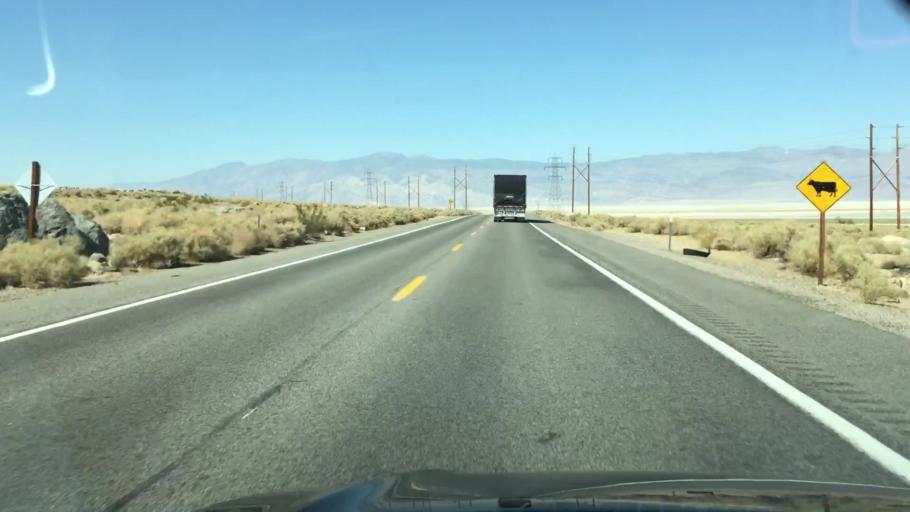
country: US
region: California
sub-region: Inyo County
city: Lone Pine
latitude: 36.3316
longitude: -118.0221
